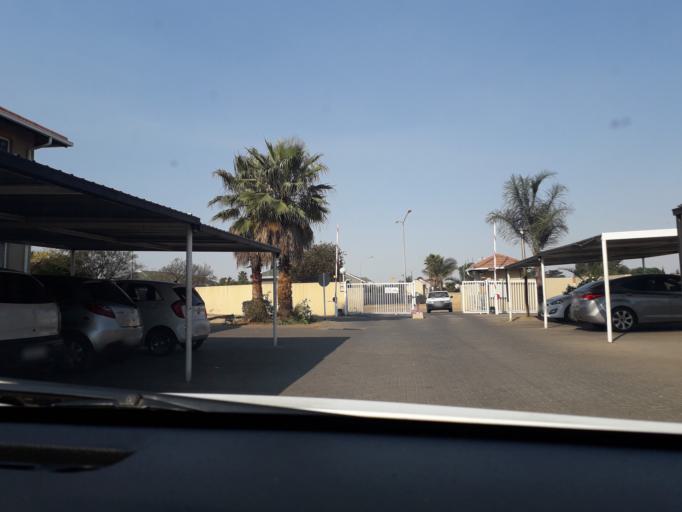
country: ZA
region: Gauteng
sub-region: City of Johannesburg Metropolitan Municipality
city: Modderfontein
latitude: -26.0818
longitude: 28.2479
